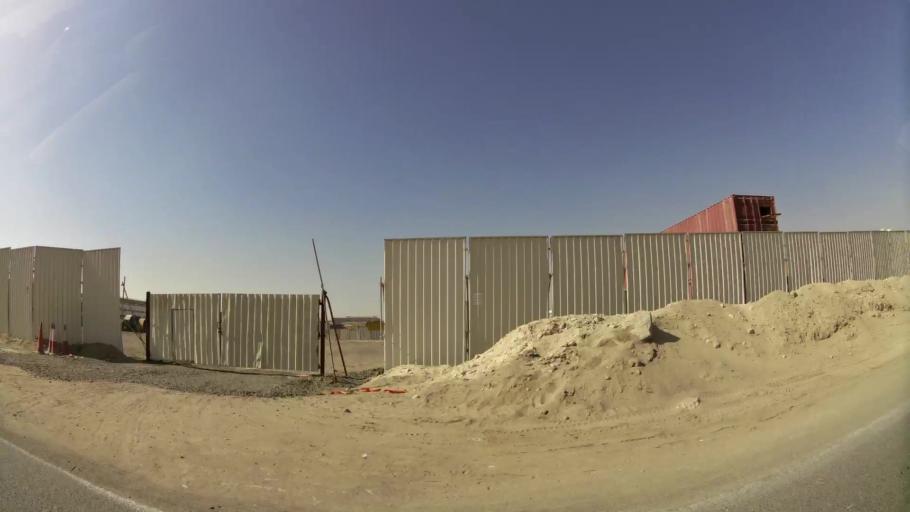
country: AE
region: Dubai
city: Dubai
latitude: 25.0035
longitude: 55.1056
